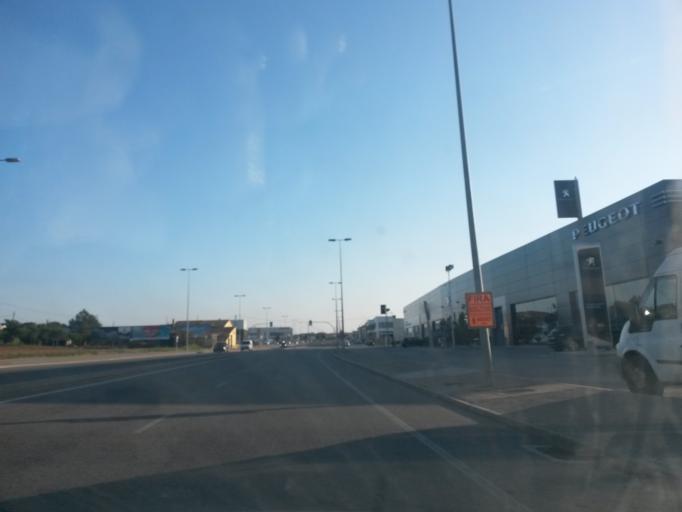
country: ES
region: Catalonia
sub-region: Provincia de Girona
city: Fornells de la Selva
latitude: 41.9381
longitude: 2.8008
